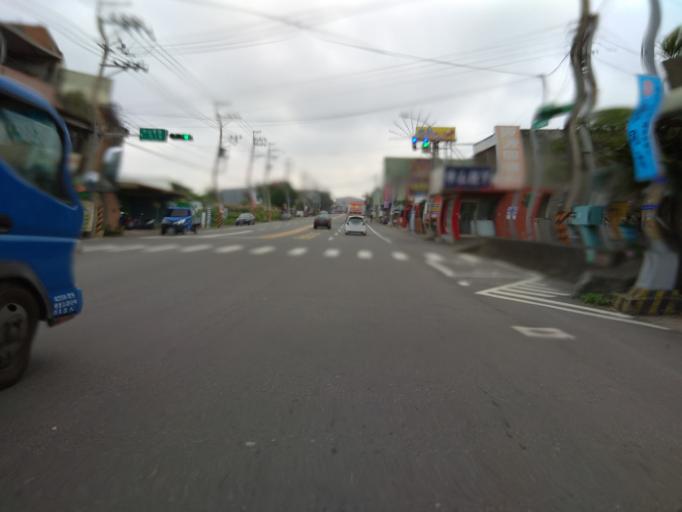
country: TW
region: Taiwan
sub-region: Hsinchu
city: Zhubei
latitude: 24.9704
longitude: 121.1125
